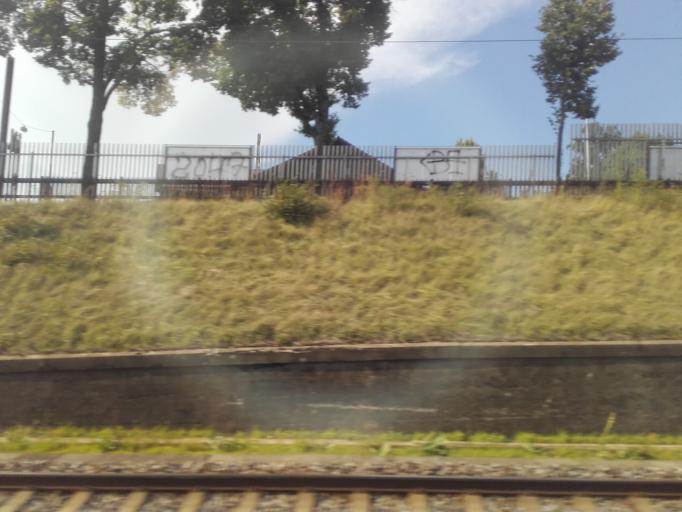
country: CH
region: Bern
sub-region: Bern-Mittelland District
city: Koniz
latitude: 46.9520
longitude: 7.4190
